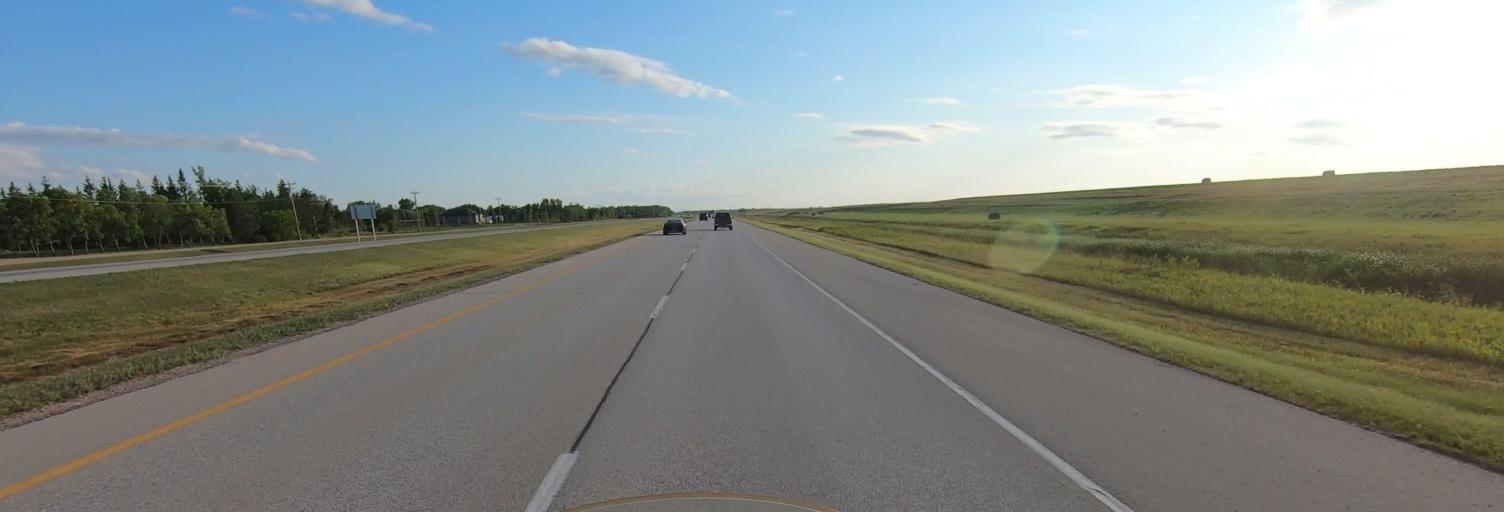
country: CA
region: Manitoba
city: Selkirk
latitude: 50.0031
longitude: -96.9633
